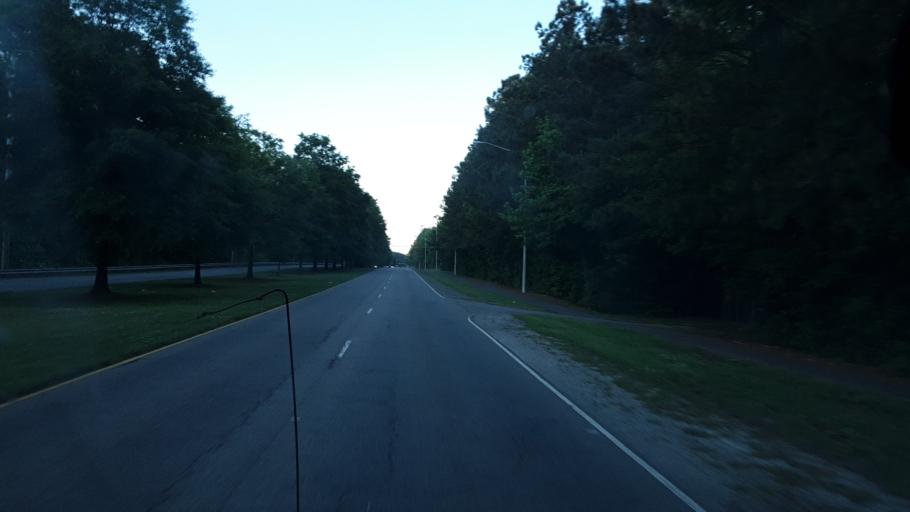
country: US
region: Virginia
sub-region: City of Virginia Beach
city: Virginia Beach
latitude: 36.8029
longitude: -75.9925
